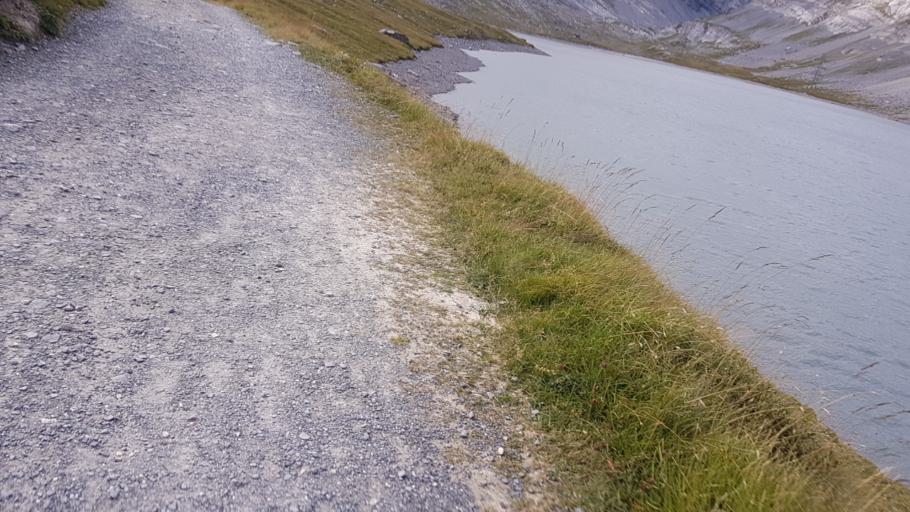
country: CH
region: Valais
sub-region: Leuk District
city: Leukerbad
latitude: 46.4147
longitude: 7.6236
